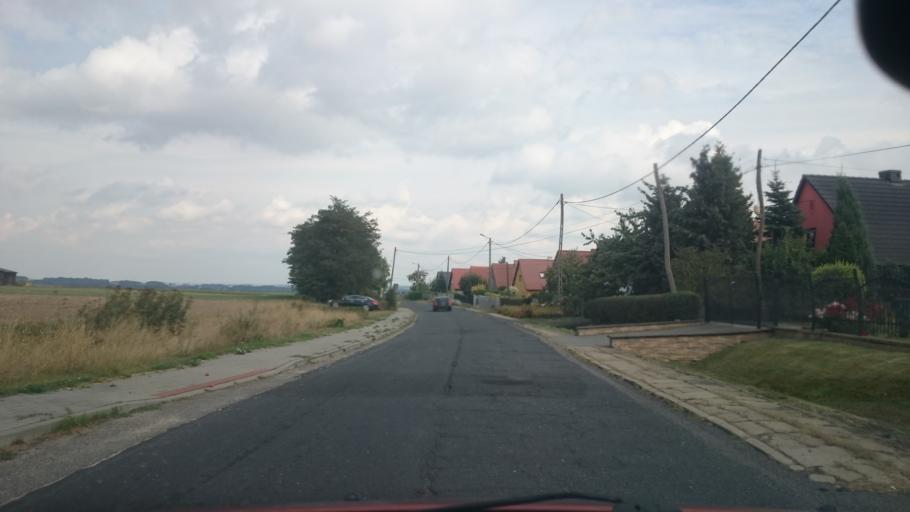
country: PL
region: Opole Voivodeship
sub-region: Powiat nyski
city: Otmuchow
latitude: 50.5064
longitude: 17.1646
